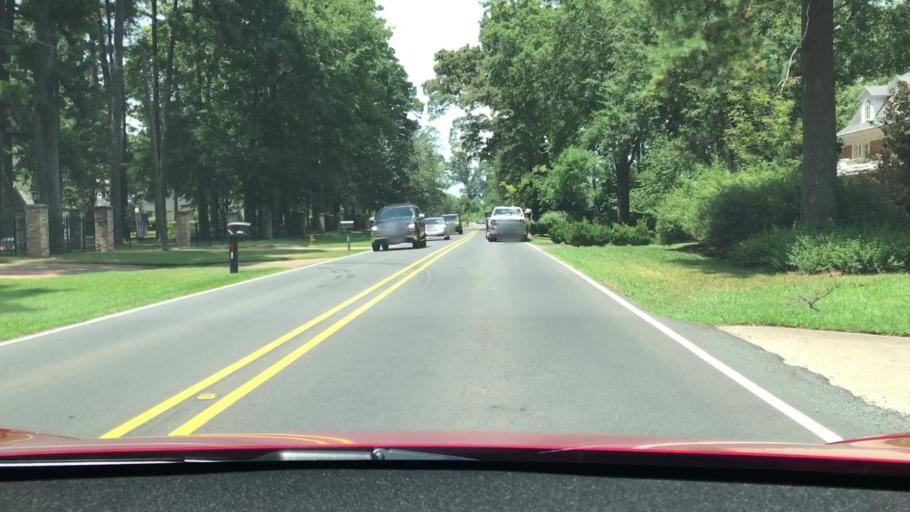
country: US
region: Louisiana
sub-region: Bossier Parish
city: Bossier City
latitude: 32.3811
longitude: -93.7138
